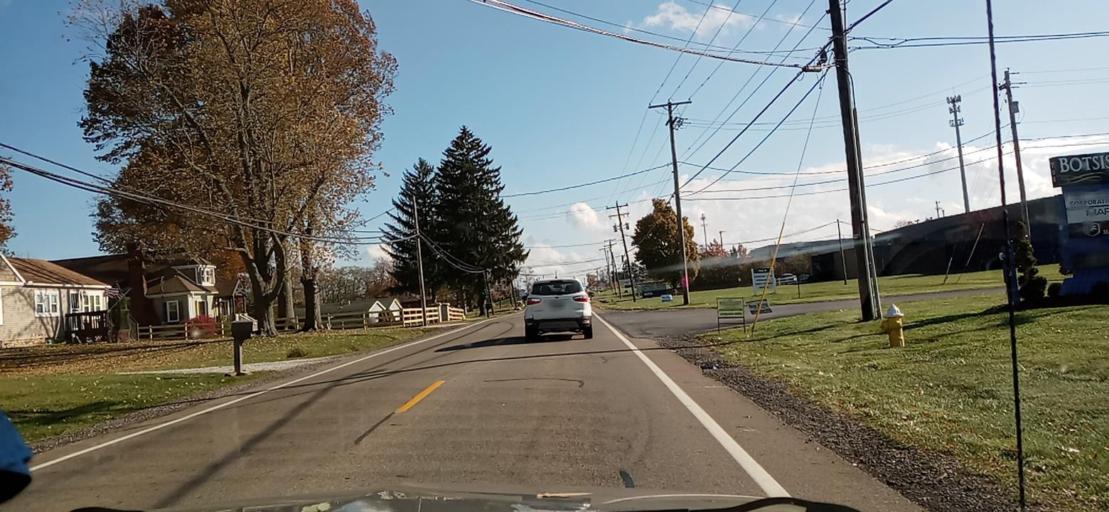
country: US
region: Ohio
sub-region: Summit County
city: Portage Lakes
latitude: 40.9975
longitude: -81.4978
